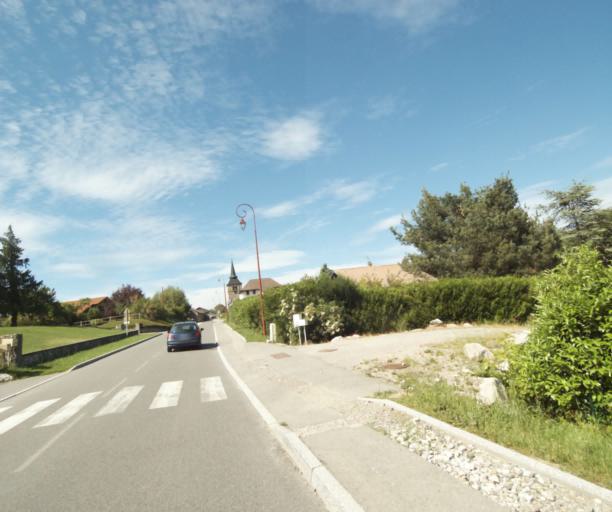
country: FR
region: Rhone-Alpes
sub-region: Departement de la Haute-Savoie
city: Perrignier
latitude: 46.3016
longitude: 6.4573
